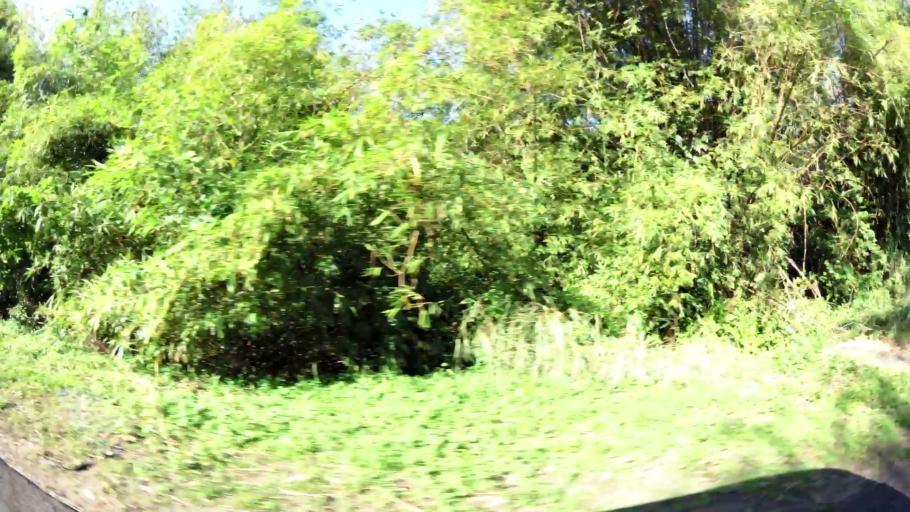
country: GF
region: Guyane
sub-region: Guyane
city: Matoury
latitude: 4.8643
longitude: -52.2738
